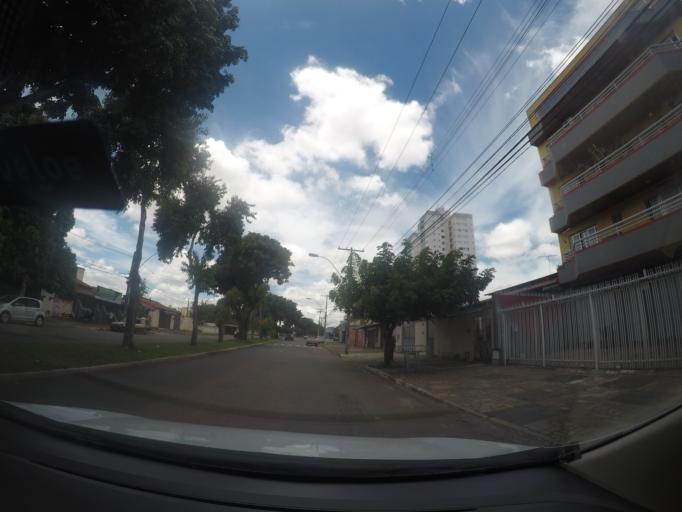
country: BR
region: Goias
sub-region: Goiania
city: Goiania
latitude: -16.6840
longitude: -49.2999
